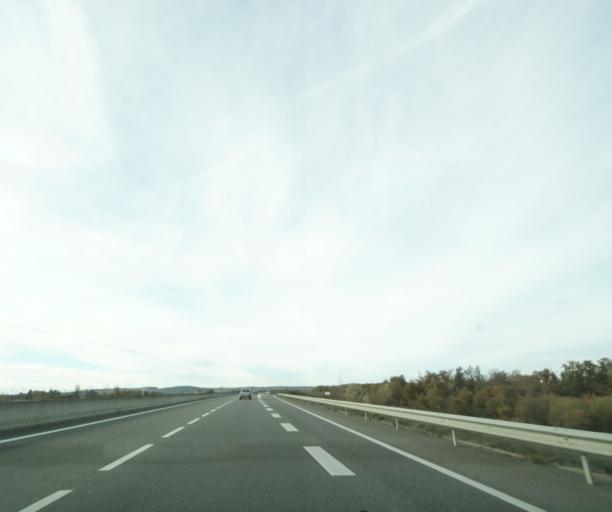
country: FR
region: Midi-Pyrenees
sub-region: Departement de la Haute-Garonne
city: Leguevin
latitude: 43.5816
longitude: 1.2229
